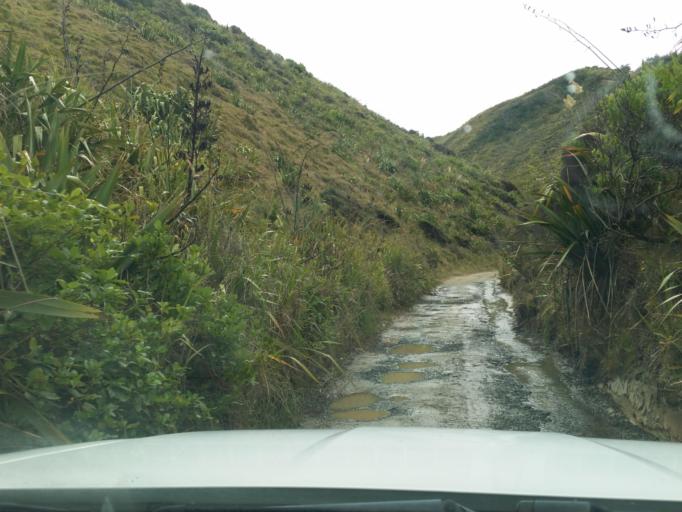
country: NZ
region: Northland
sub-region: Kaipara District
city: Dargaville
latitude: -36.0040
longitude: 173.7938
